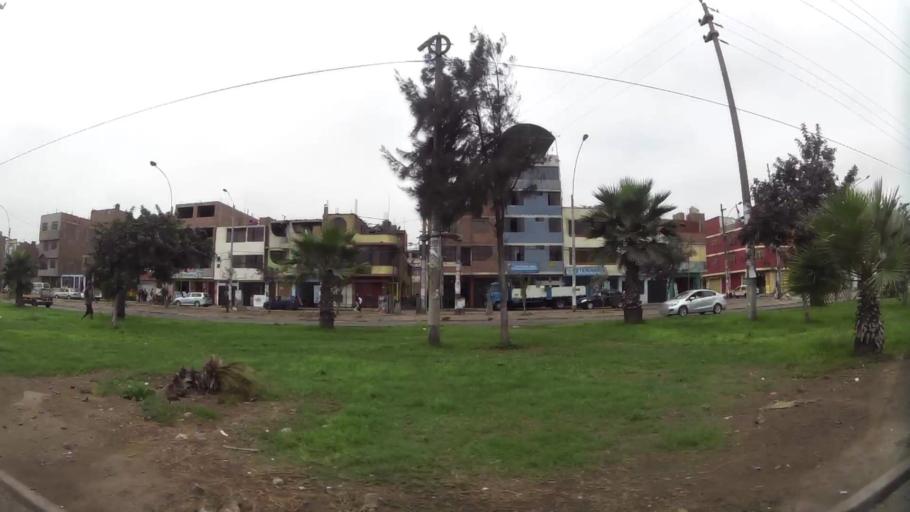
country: PE
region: Lima
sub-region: Lima
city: Independencia
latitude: -12.0097
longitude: -77.0815
